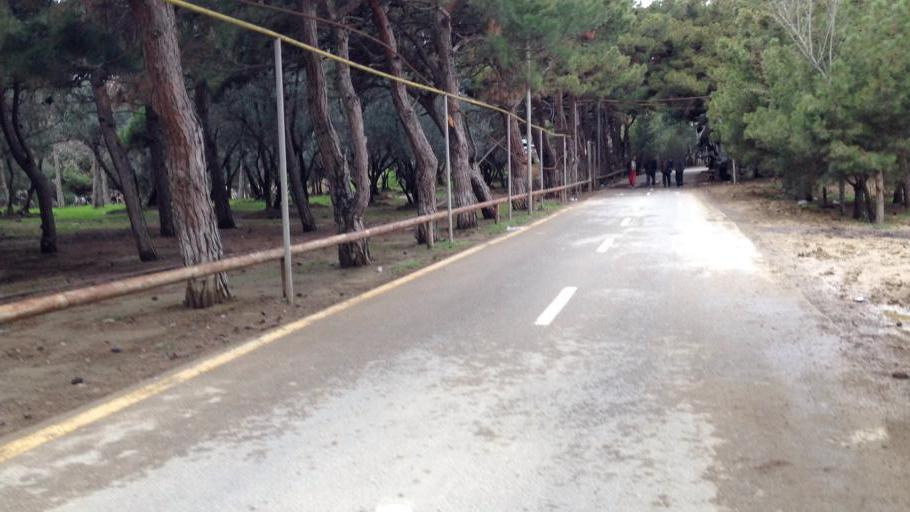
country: AZ
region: Baki
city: Baku
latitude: 40.3950
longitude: 49.8548
